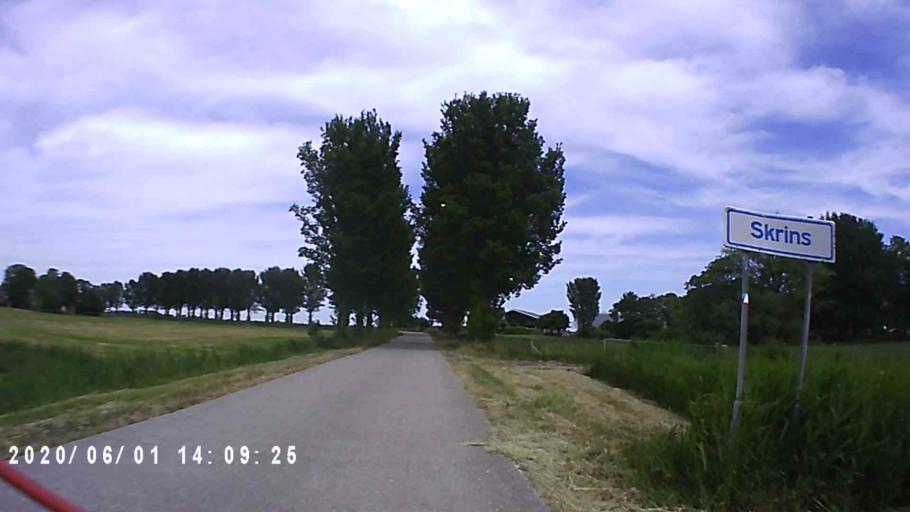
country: NL
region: Friesland
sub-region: Gemeente Littenseradiel
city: Winsum
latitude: 53.1226
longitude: 5.6460
